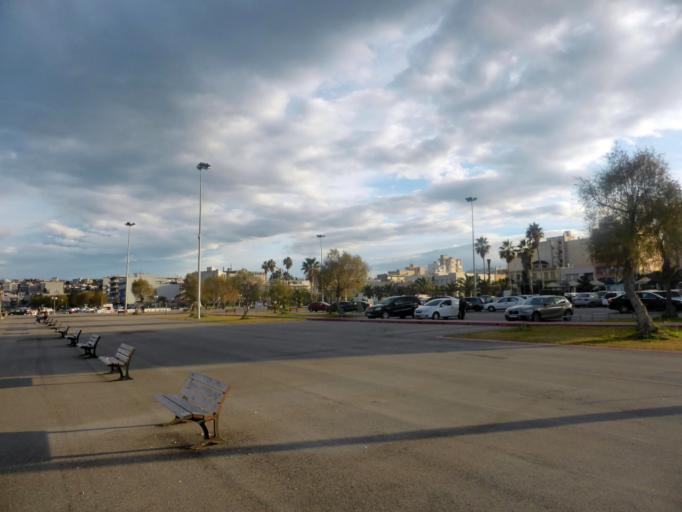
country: GR
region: Peloponnese
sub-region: Nomos Korinthias
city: Korinthos
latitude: 37.9420
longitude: 22.9341
